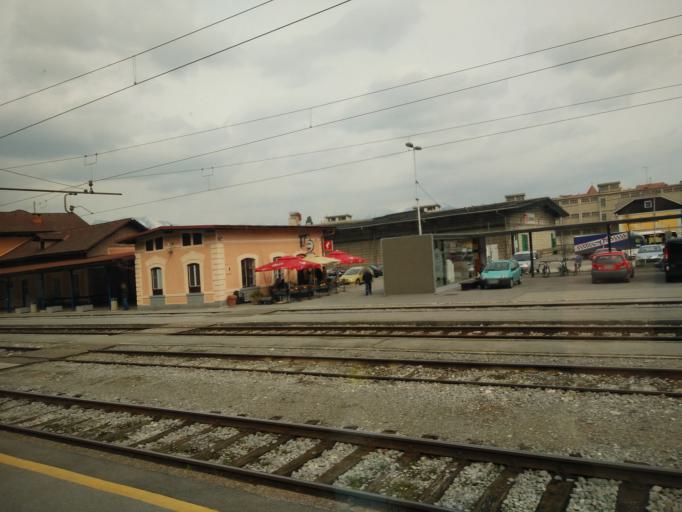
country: SI
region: Kranj
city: Kranj
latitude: 46.2385
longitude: 14.3482
